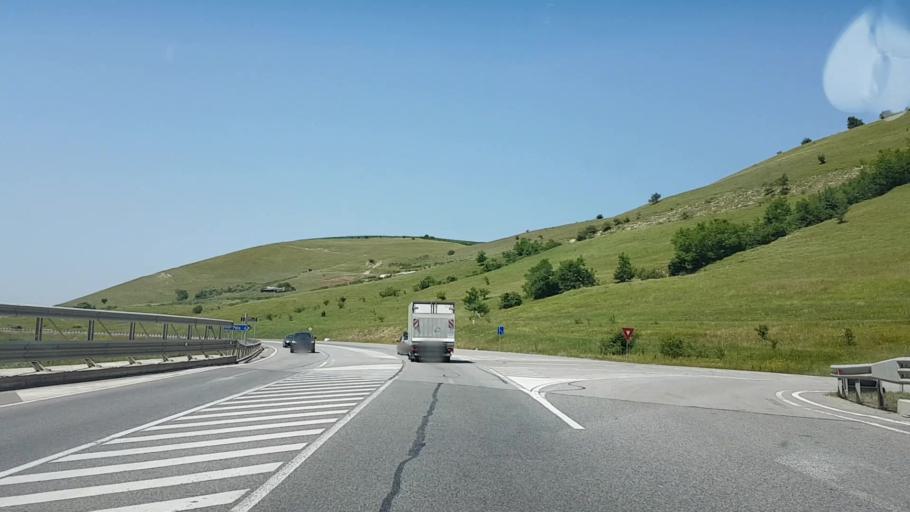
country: RO
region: Cluj
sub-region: Comuna Apahida
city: Dezmir
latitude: 46.7454
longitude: 23.7121
